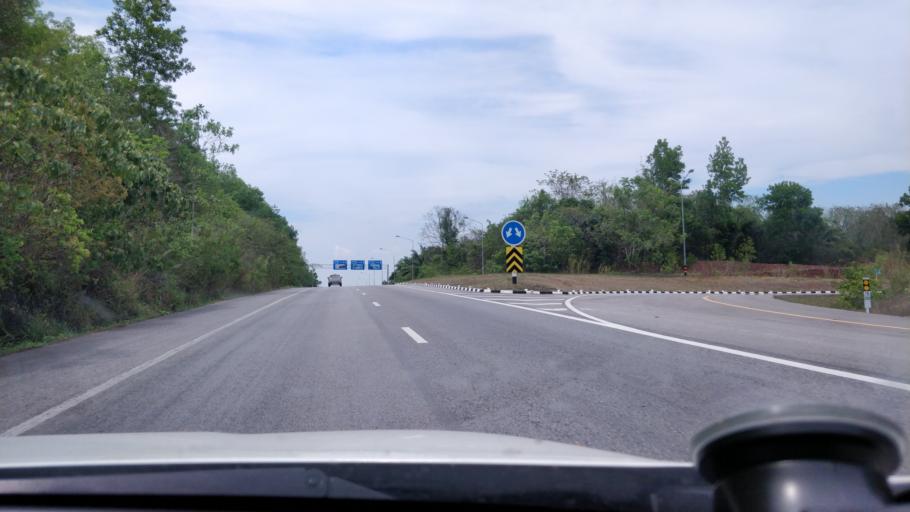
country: TH
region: Surat Thani
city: Khian Sa
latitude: 8.8135
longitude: 99.1669
